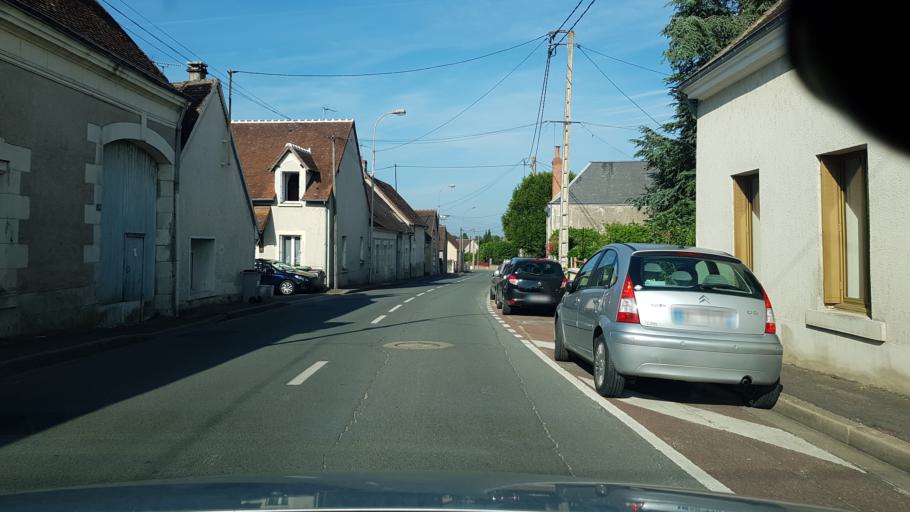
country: FR
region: Centre
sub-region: Departement du Loir-et-Cher
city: Selles-sur-Cher
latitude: 47.2805
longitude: 1.5652
